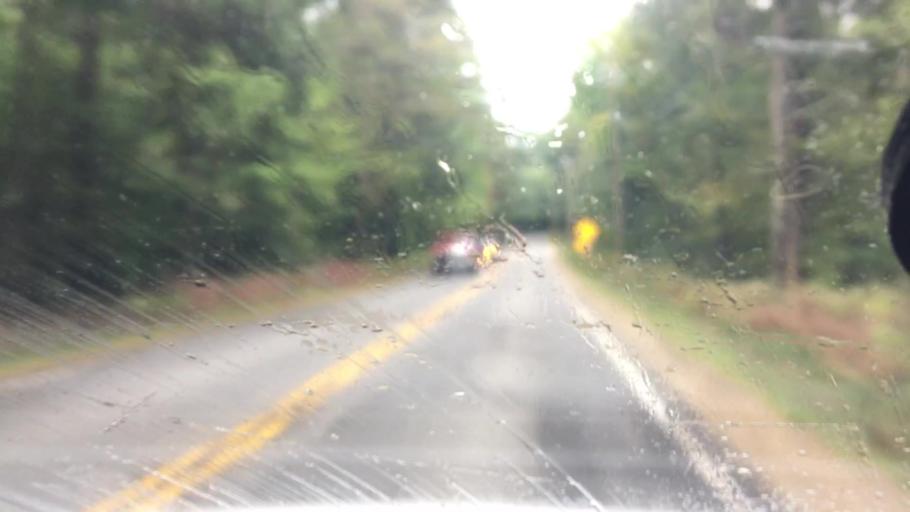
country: US
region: New Hampshire
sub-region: Carroll County
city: Wakefield
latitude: 43.5773
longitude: -71.0197
